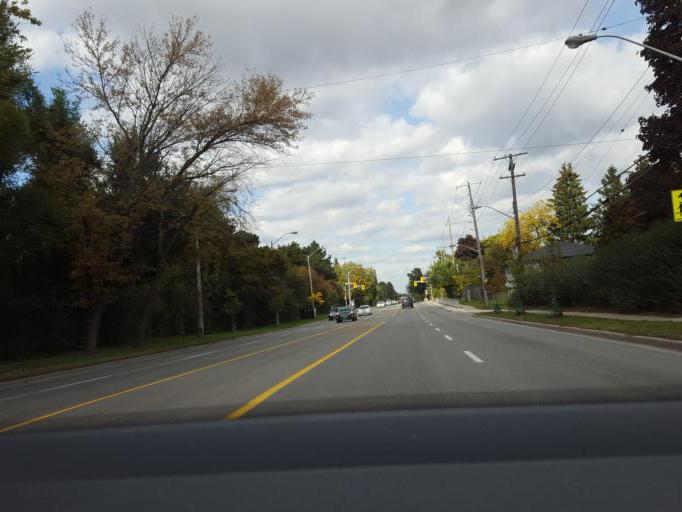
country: CA
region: Ontario
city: Willowdale
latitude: 43.7449
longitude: -79.3582
